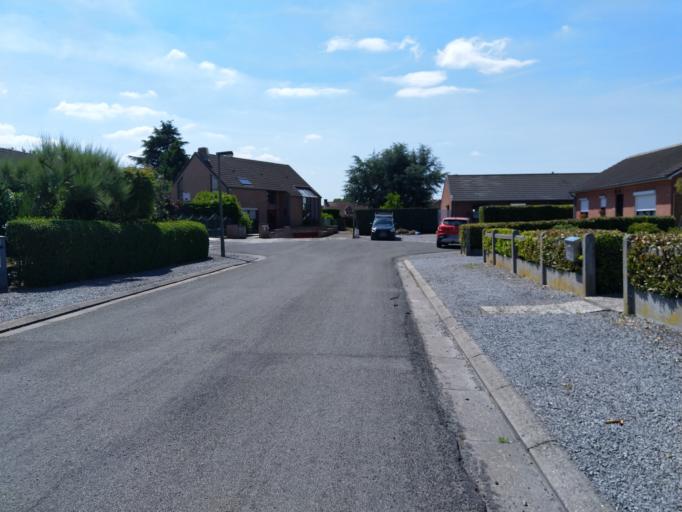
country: BE
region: Wallonia
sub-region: Province du Hainaut
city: Saint-Ghislain
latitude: 50.4737
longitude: 3.8191
